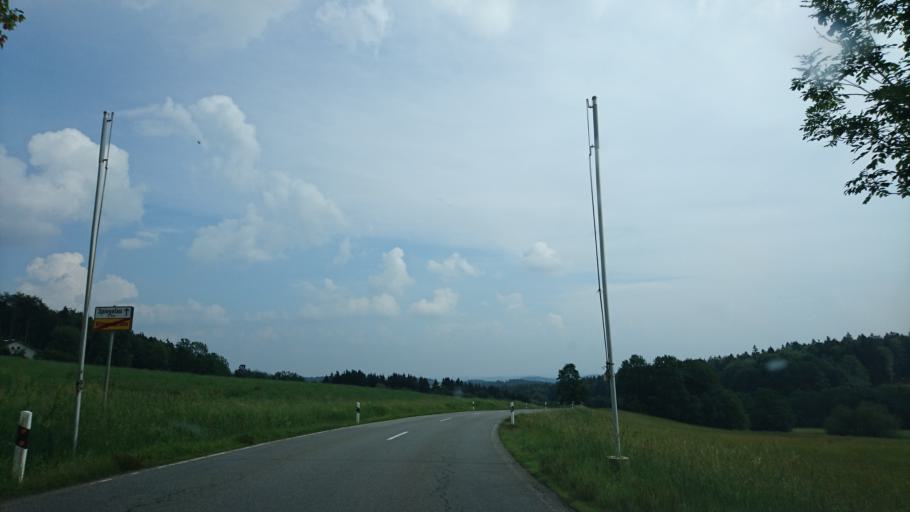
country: DE
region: Bavaria
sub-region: Lower Bavaria
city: Eppenschlag
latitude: 48.9205
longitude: 13.3223
